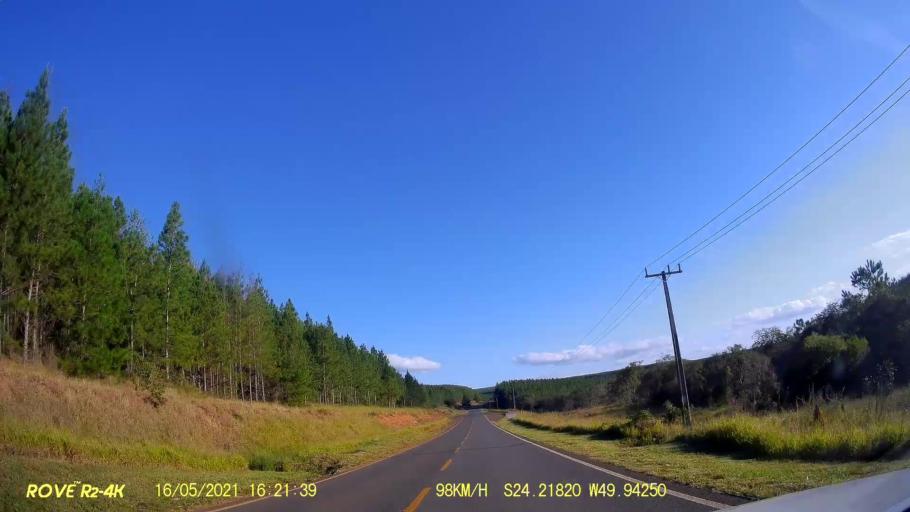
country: BR
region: Parana
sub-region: Jaguariaiva
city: Jaguariaiva
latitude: -24.2183
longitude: -49.9426
